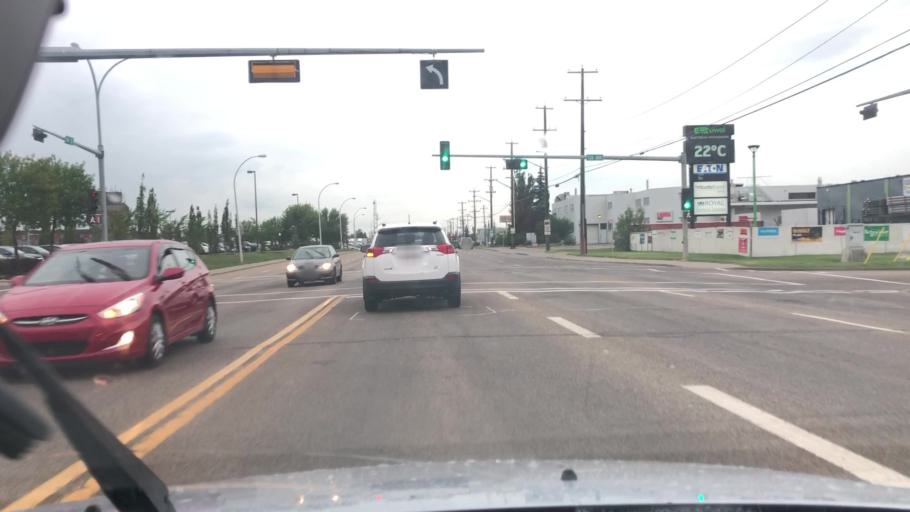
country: CA
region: Alberta
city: St. Albert
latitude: 53.5787
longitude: -113.5780
